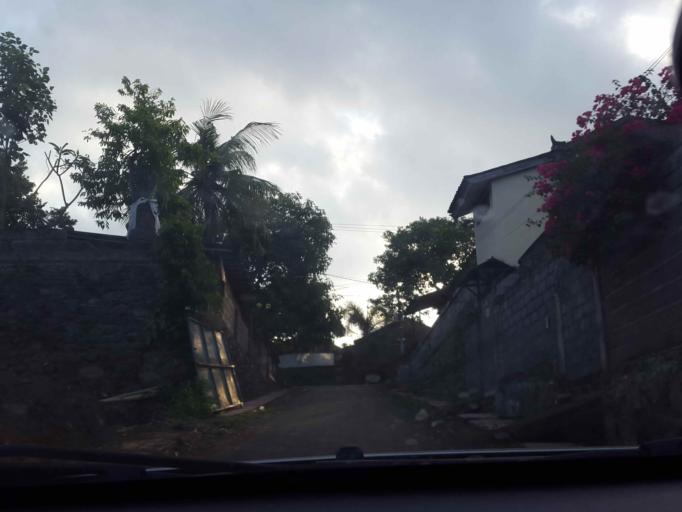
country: ID
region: Bali
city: Semarapura
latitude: -8.5392
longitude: 115.4156
